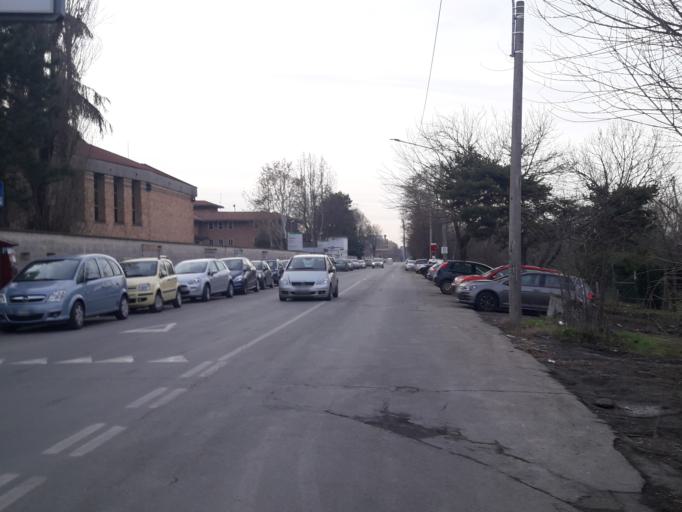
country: IT
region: Emilia-Romagna
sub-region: Provincia di Bologna
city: Bologna
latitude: 44.5065
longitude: 11.3158
